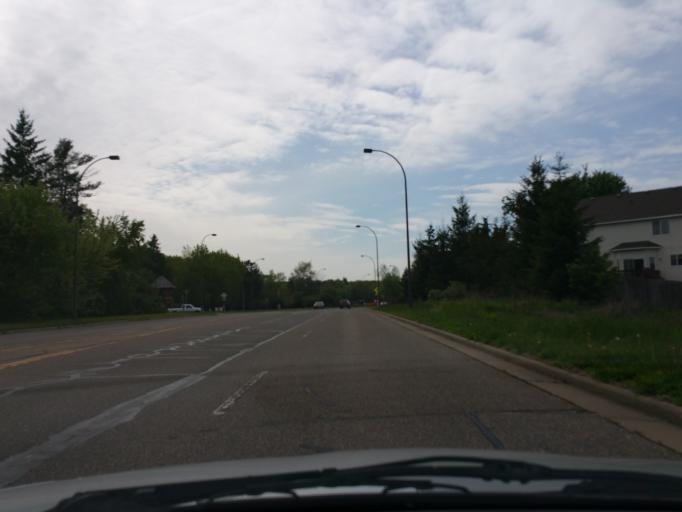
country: US
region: Wisconsin
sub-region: Saint Croix County
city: Hudson
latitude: 44.9591
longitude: -92.7002
